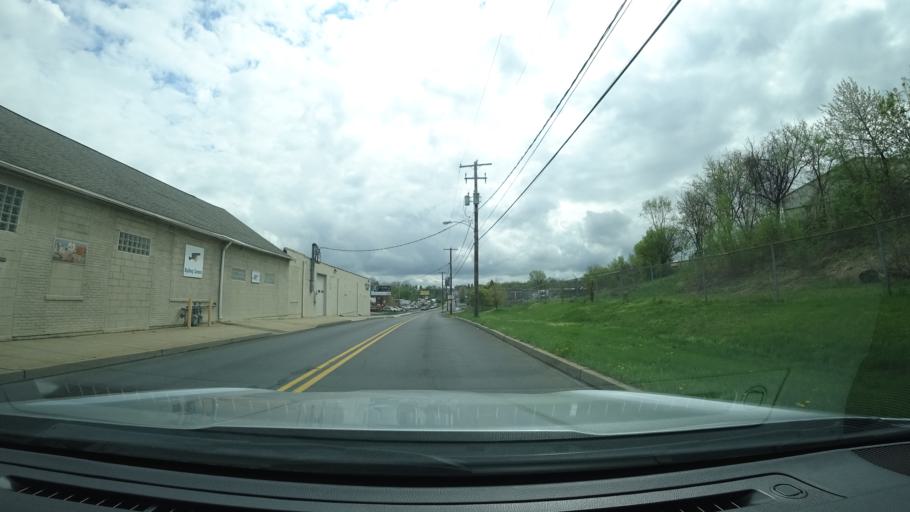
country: US
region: Pennsylvania
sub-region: Lehigh County
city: Fullerton
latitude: 40.6187
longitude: -75.4697
